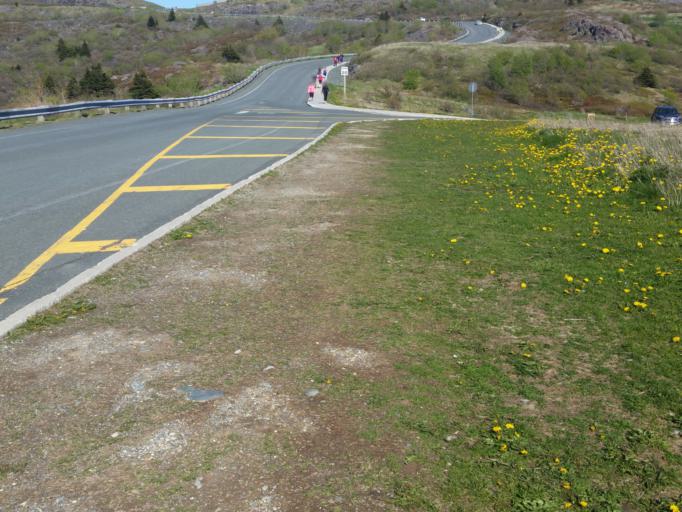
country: CA
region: Newfoundland and Labrador
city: St. John's
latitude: 47.5713
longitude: -52.6867
